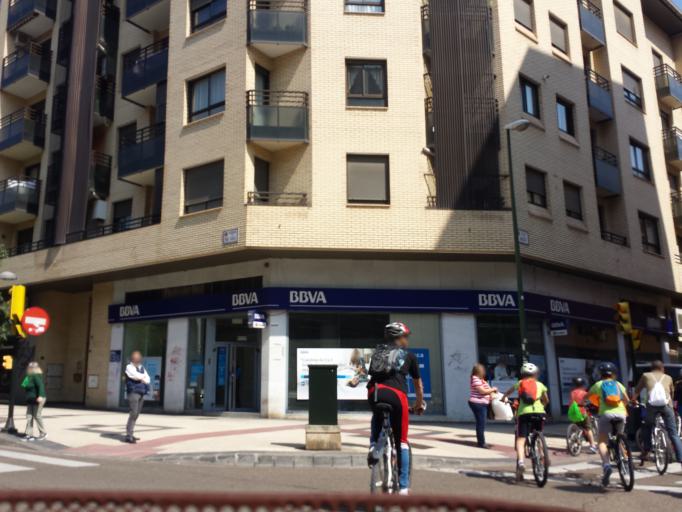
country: ES
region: Aragon
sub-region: Provincia de Zaragoza
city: Almozara
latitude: 41.6604
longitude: -0.8987
